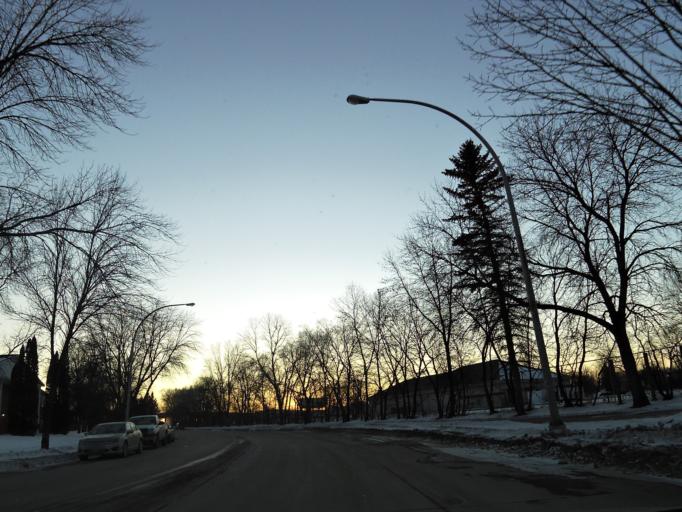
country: US
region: North Dakota
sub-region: Grand Forks County
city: Grand Forks
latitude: 47.9216
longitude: -97.0336
